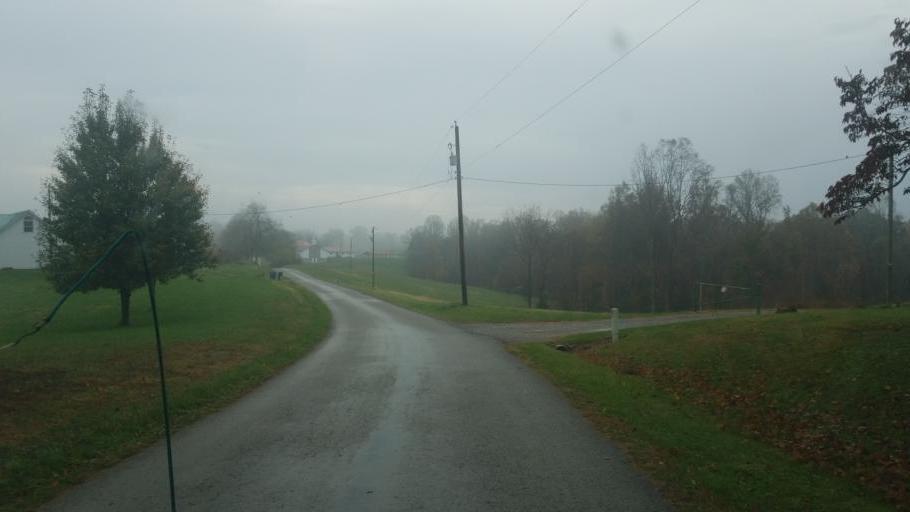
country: US
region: Ohio
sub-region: Morgan County
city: McConnelsville
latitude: 39.5004
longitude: -81.8208
